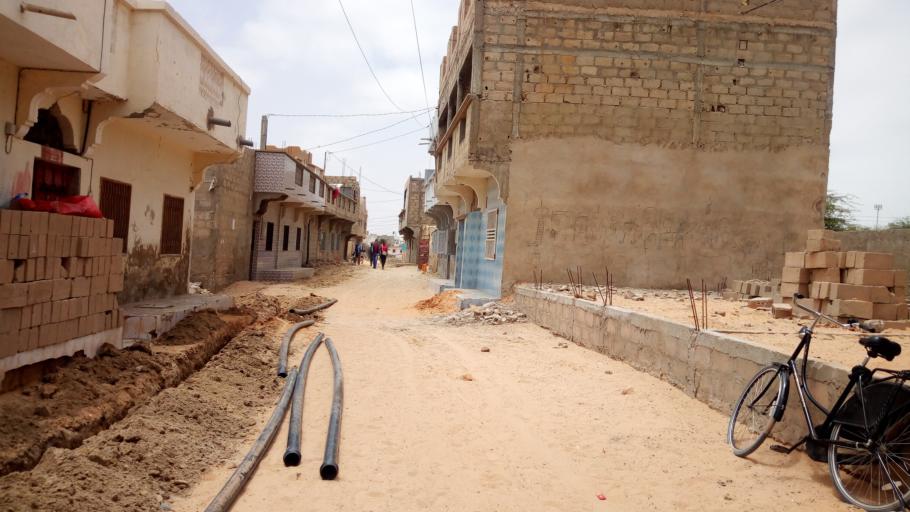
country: SN
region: Saint-Louis
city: Saint-Louis
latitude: 16.0136
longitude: -16.4861
